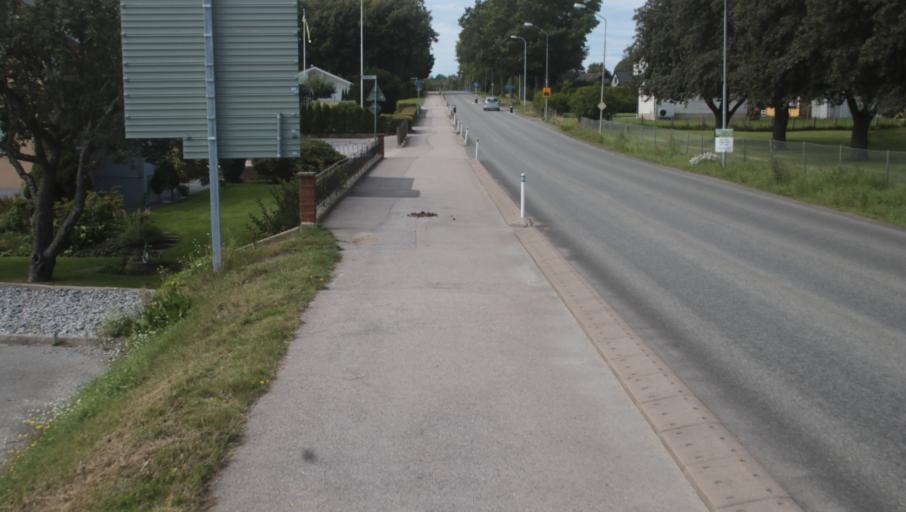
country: SE
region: Blekinge
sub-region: Karlshamns Kommun
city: Karlshamn
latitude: 56.1997
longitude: 14.8347
